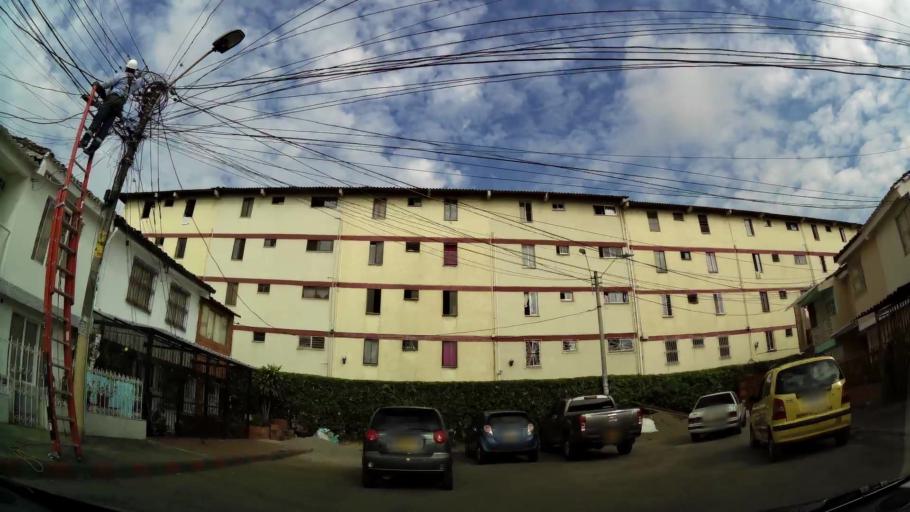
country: CO
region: Valle del Cauca
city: Cali
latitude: 3.4812
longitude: -76.4915
